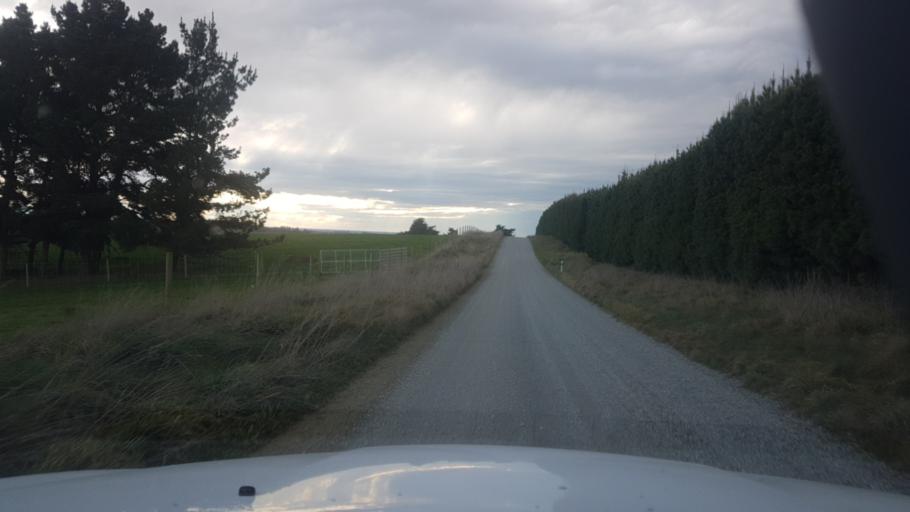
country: NZ
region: Canterbury
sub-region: Timaru District
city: Pleasant Point
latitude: -44.3406
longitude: 171.1436
